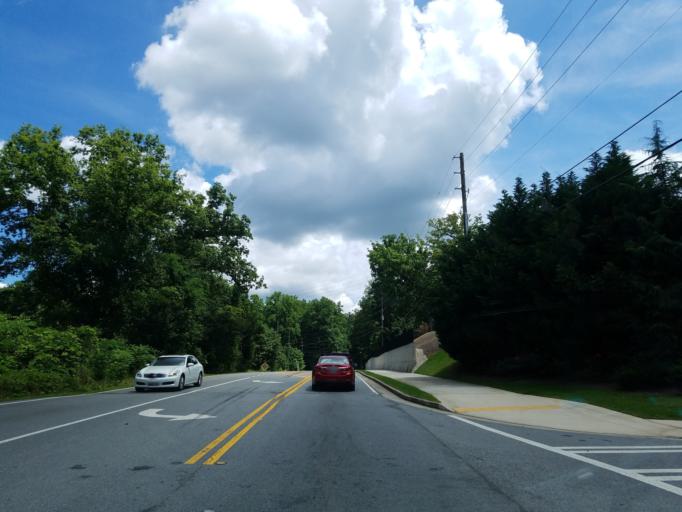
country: US
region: Georgia
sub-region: Cobb County
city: Kennesaw
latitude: 33.9912
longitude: -84.5949
